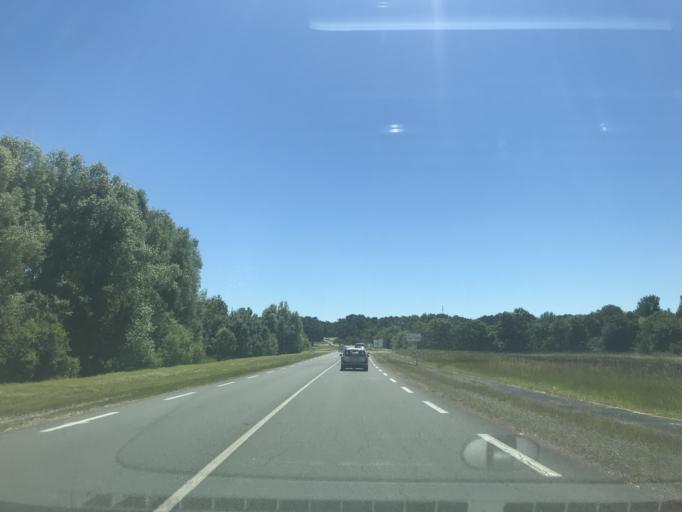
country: FR
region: Poitou-Charentes
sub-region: Departement de la Charente-Maritime
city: Saint-Georges-de-Didonne
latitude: 45.6006
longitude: -0.9736
